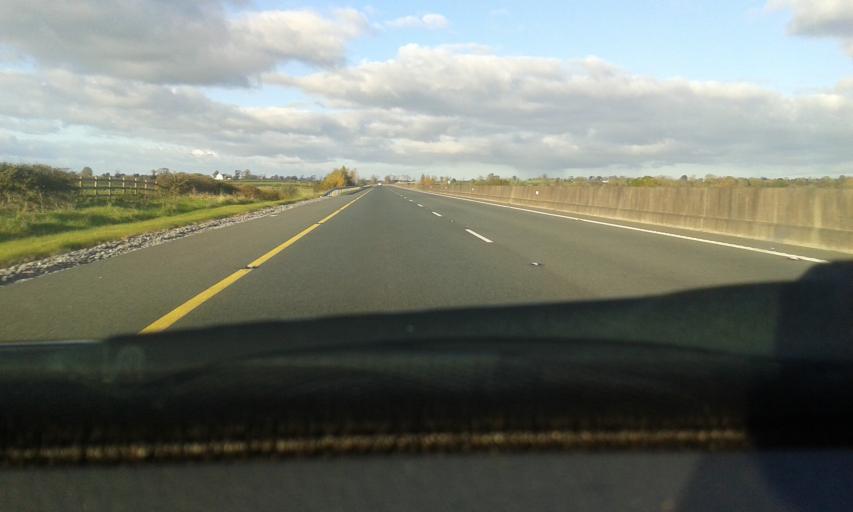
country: IE
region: Munster
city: Cahir
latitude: 52.4334
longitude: -7.9133
